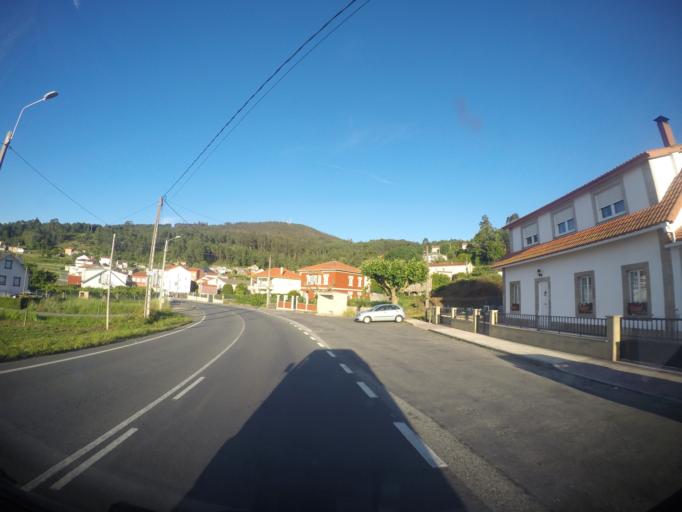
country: ES
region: Galicia
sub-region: Provincia da Coruna
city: Noia
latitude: 42.7740
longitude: -8.9316
